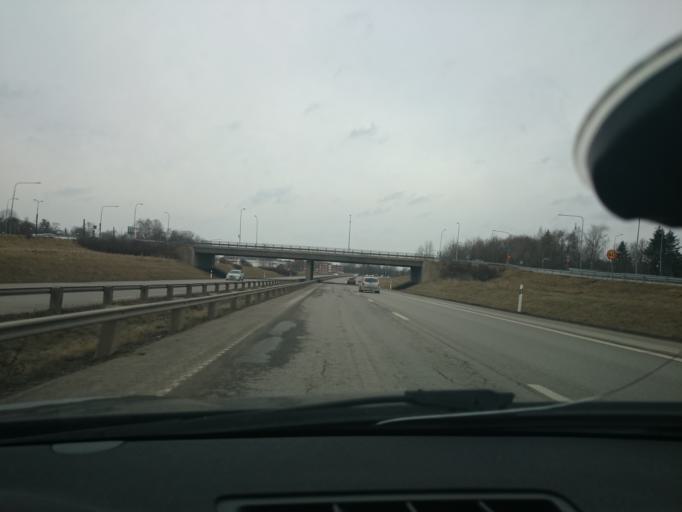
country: SE
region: OEstergoetland
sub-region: Norrkopings Kommun
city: Norrkoping
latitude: 58.5651
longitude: 16.2209
